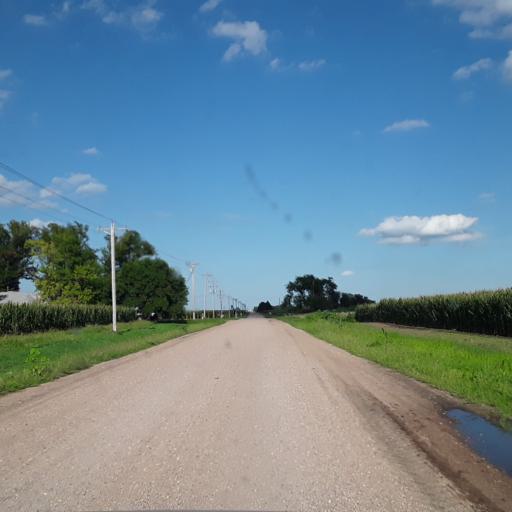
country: US
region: Nebraska
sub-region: Hall County
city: Wood River
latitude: 40.9167
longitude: -98.5651
